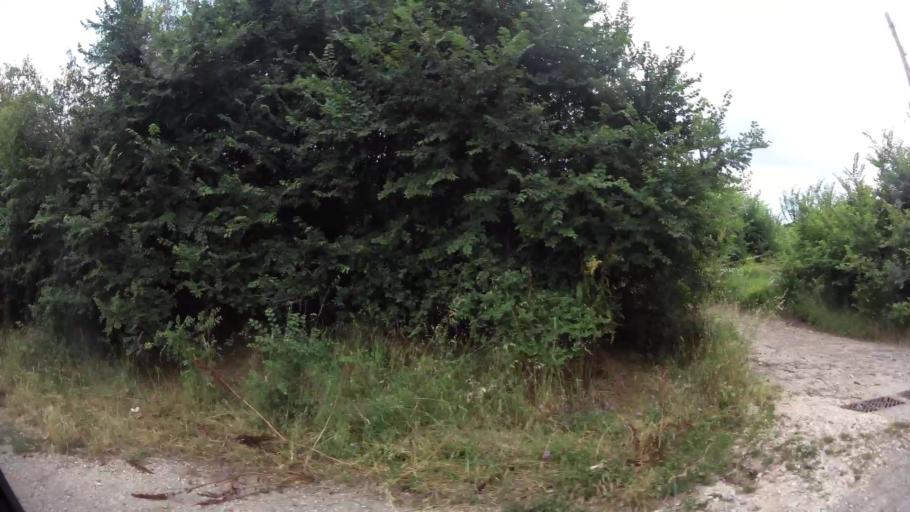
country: GR
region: West Macedonia
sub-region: Nomos Kozanis
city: Koila
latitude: 40.3478
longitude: 21.8302
